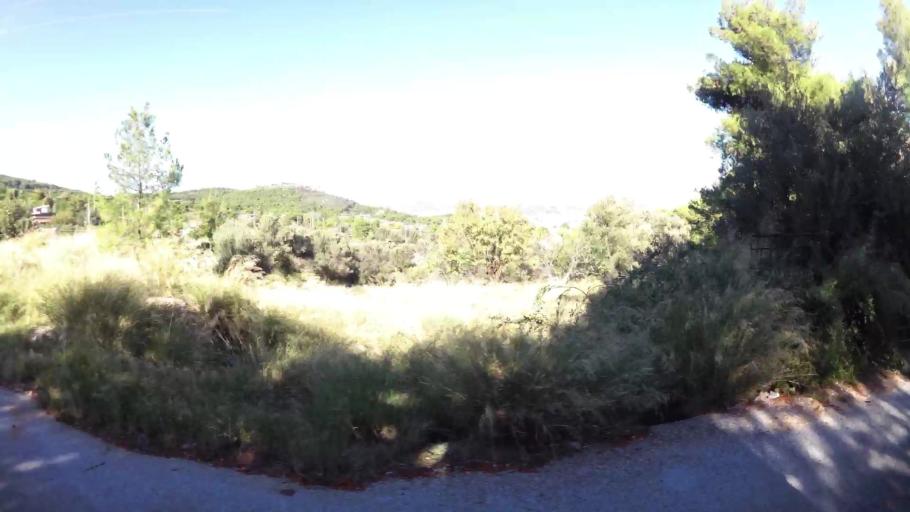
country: GR
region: Attica
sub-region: Nomarchia Anatolikis Attikis
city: Leondarion
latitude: 37.9919
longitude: 23.8420
